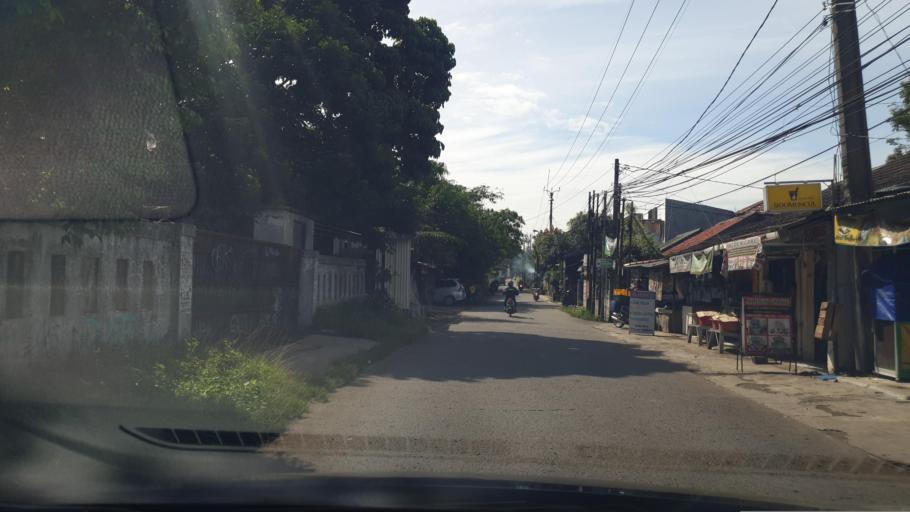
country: ID
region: West Java
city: Sawangan
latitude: -6.4071
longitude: 106.7785
